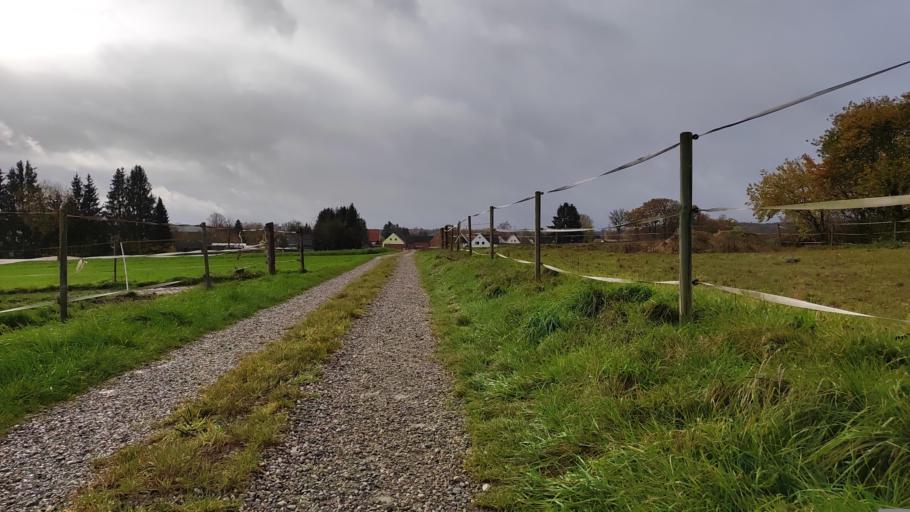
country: DE
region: Bavaria
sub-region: Swabia
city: Dinkelscherben
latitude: 48.3430
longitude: 10.5497
